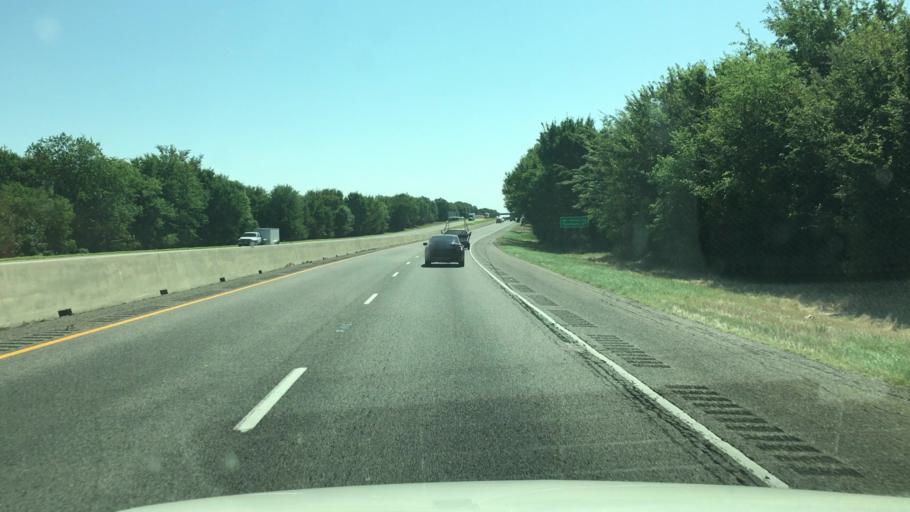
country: US
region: Texas
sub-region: Franklin County
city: Mount Vernon
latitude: 33.1659
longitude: -95.3912
